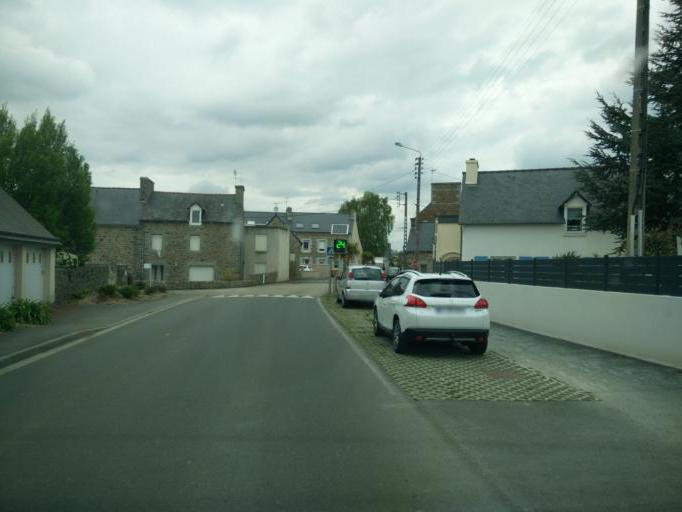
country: FR
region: Brittany
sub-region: Departement des Cotes-d'Armor
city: Yffiniac
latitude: 48.4914
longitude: -2.6838
